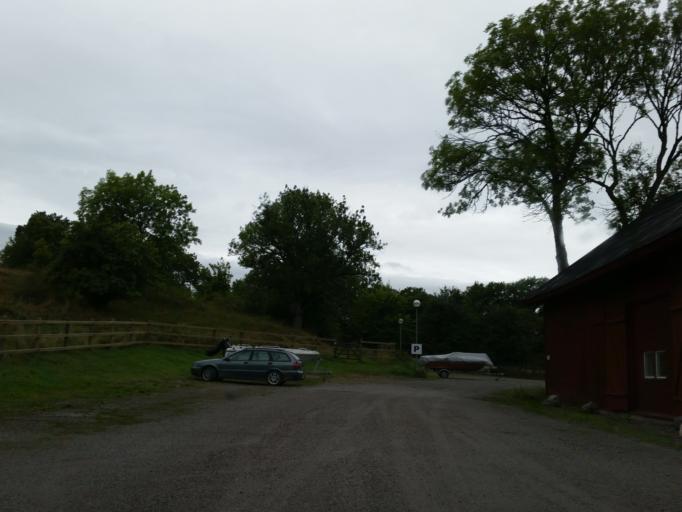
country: SE
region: Uppsala
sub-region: Habo Kommun
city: Balsta
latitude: 59.6630
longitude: 17.4853
